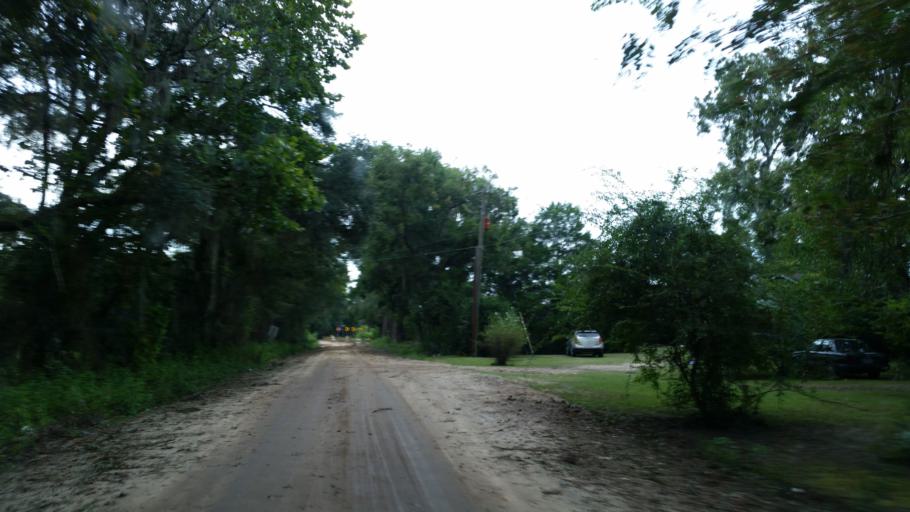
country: US
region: Georgia
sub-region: Lowndes County
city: Valdosta
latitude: 30.7304
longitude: -83.2831
